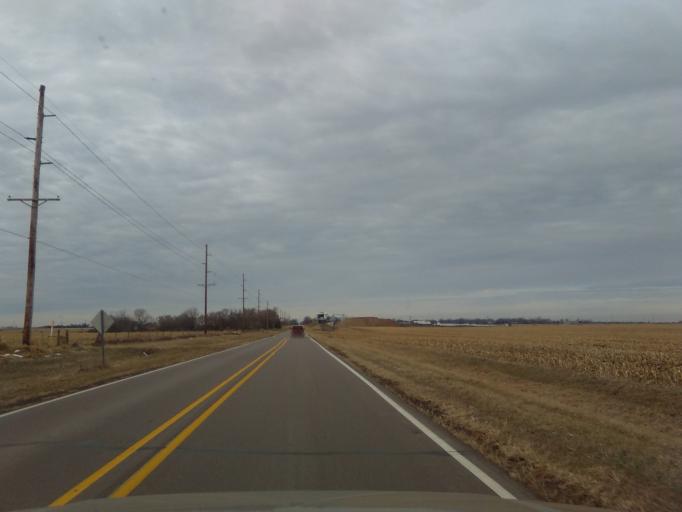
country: US
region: Nebraska
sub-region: Hall County
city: Grand Island
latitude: 40.7710
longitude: -98.3454
